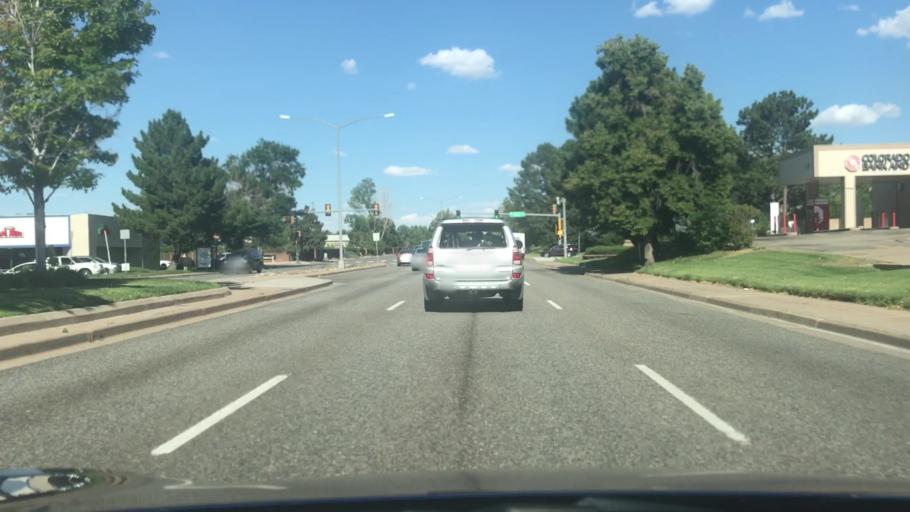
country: US
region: Colorado
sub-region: Arapahoe County
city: Dove Valley
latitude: 39.6530
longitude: -104.8085
